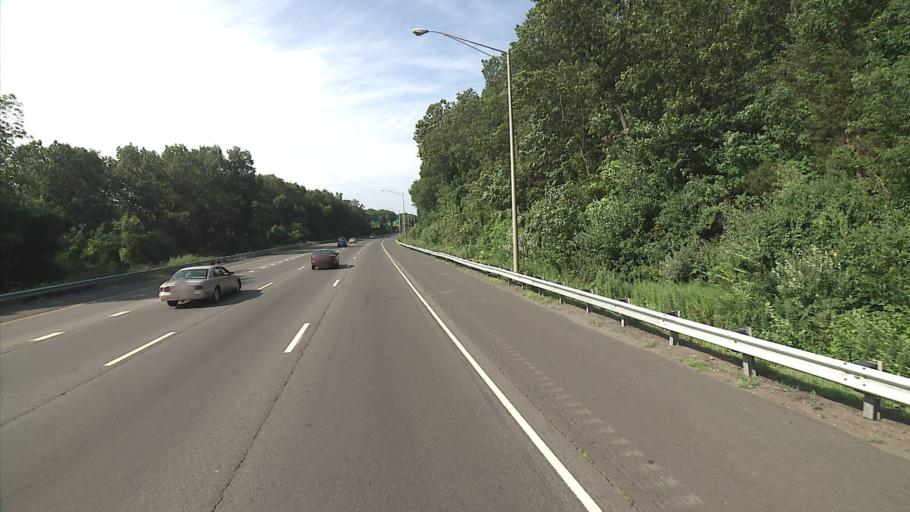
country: US
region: Connecticut
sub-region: Middlesex County
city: Cromwell
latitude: 41.6357
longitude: -72.6846
